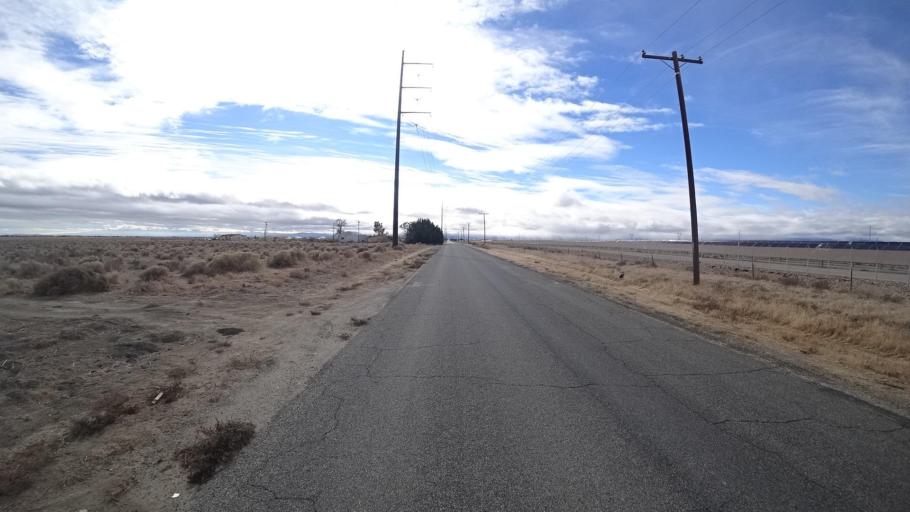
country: US
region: California
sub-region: Kern County
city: Rosamond
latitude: 34.8471
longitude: -118.3088
